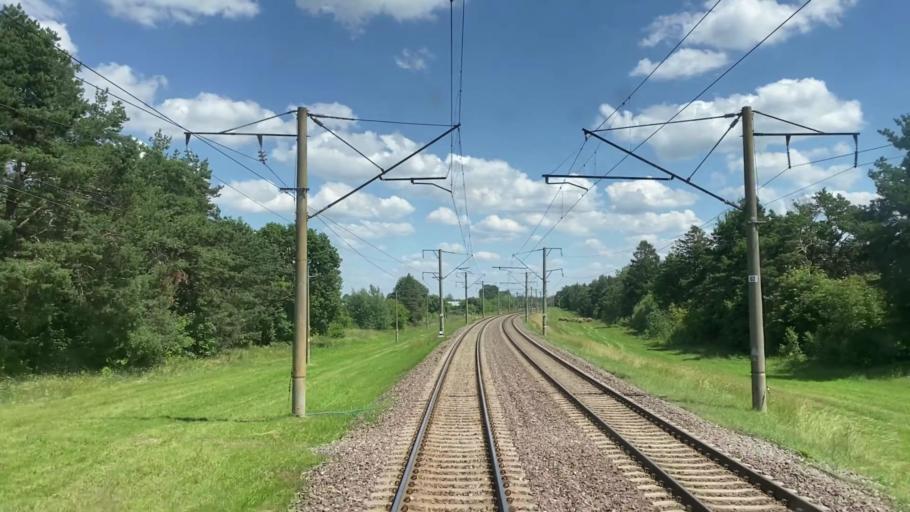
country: BY
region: Brest
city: Ivatsevichy
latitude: 52.6924
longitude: 25.3046
